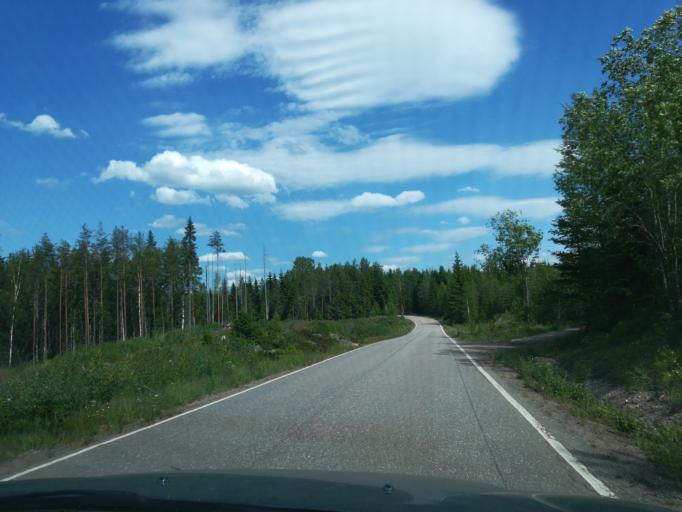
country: FI
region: South Karelia
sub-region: Imatra
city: Ruokolahti
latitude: 61.4694
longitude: 28.8257
